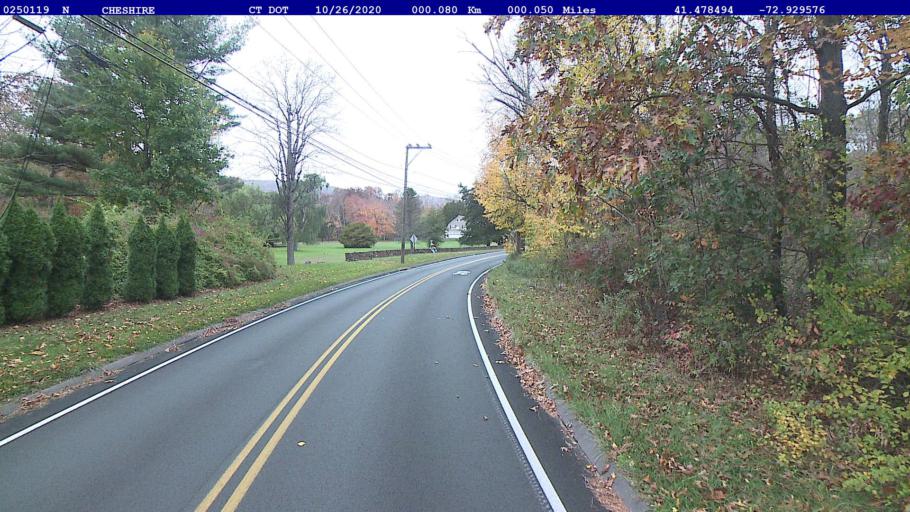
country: US
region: Connecticut
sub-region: New Haven County
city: Cheshire
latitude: 41.4785
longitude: -72.9296
